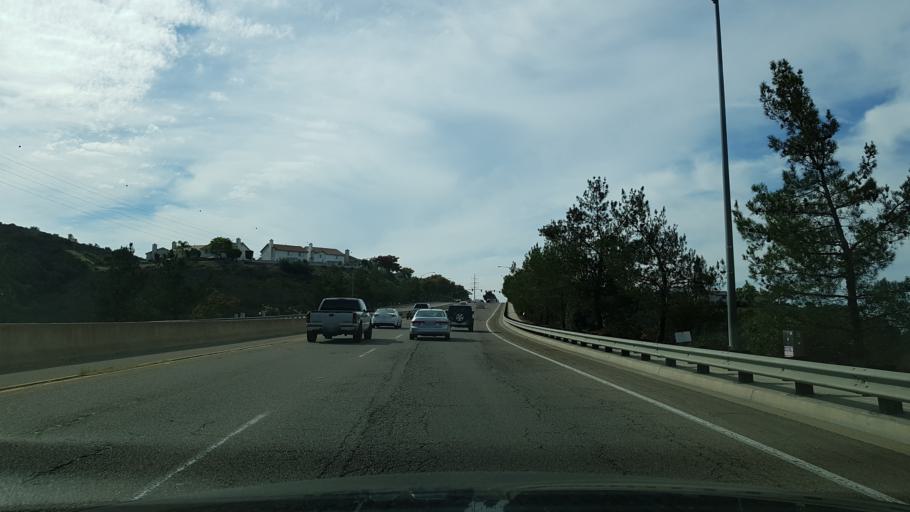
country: US
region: California
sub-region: San Diego County
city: Poway
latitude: 32.9344
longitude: -117.0740
